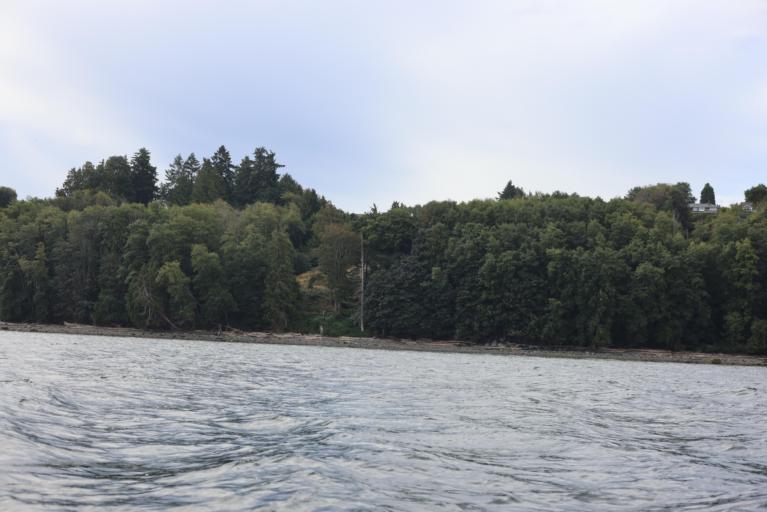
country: CA
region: British Columbia
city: Nanaimo
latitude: 49.2519
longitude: -124.0386
